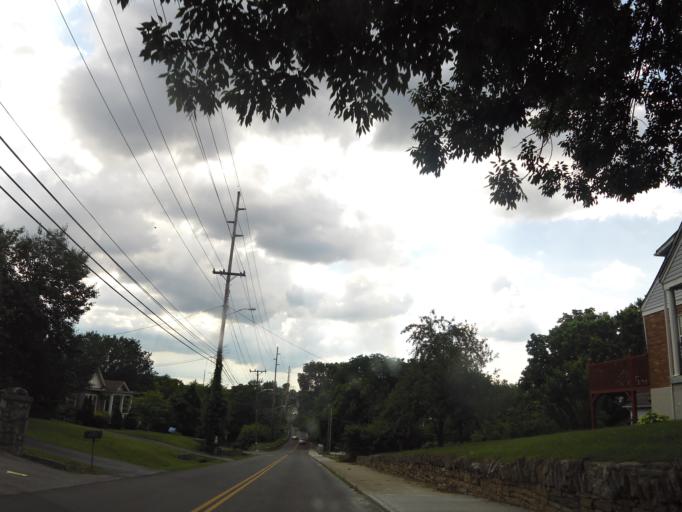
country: US
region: Tennessee
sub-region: Davidson County
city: Nashville
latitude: 36.1822
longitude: -86.7306
